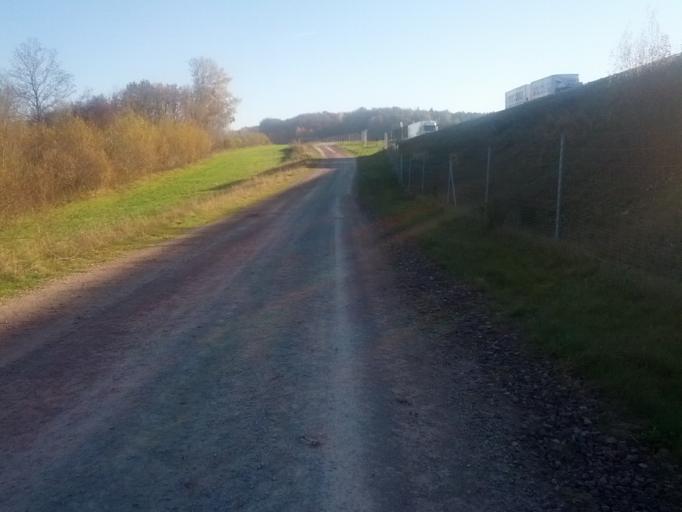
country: DE
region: Thuringia
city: Mechterstadt
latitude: 50.9424
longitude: 10.4905
